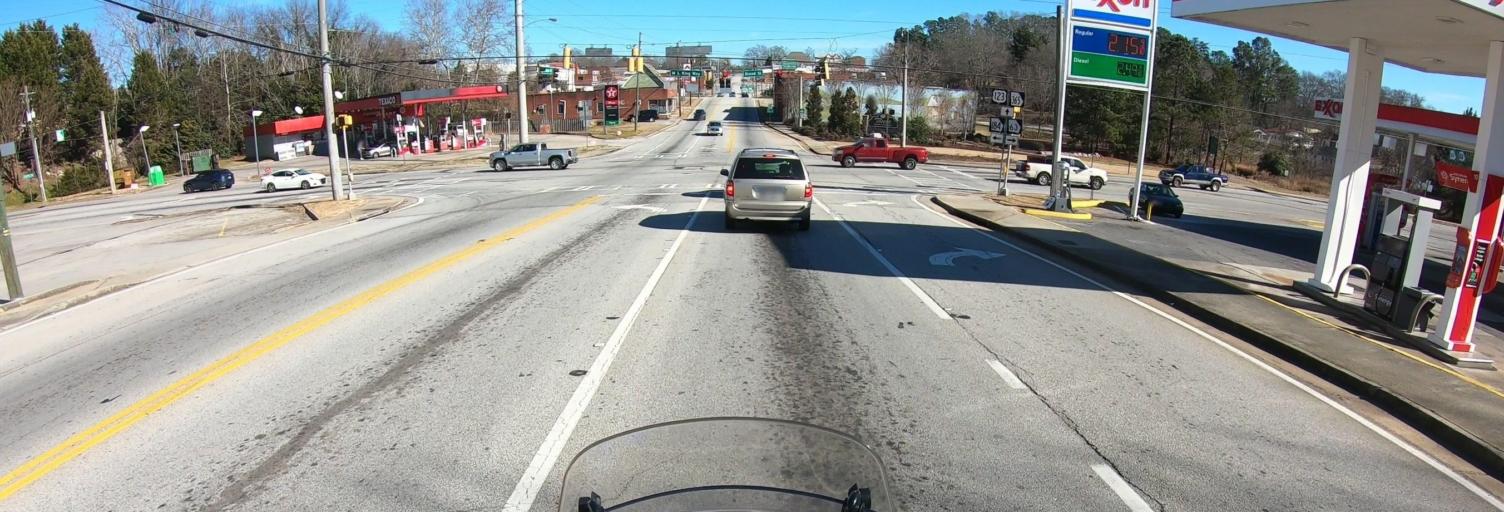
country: US
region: Georgia
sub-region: Stephens County
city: Toccoa
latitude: 34.5773
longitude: -83.3336
